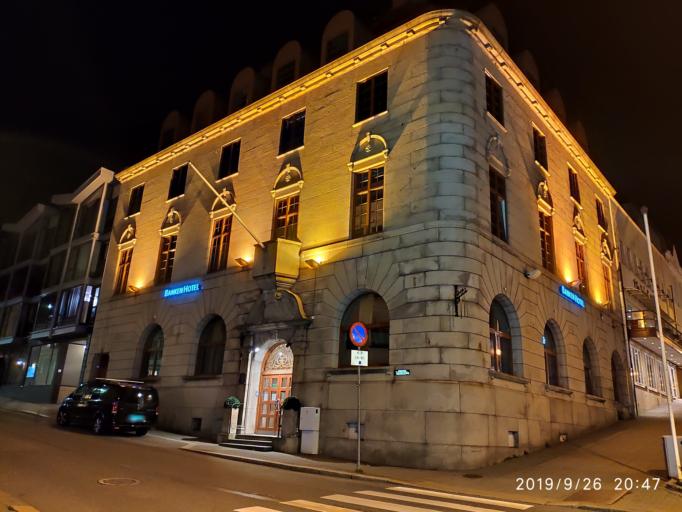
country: NO
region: Rogaland
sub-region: Haugesund
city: Haugesund
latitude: 59.4135
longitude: 5.2672
